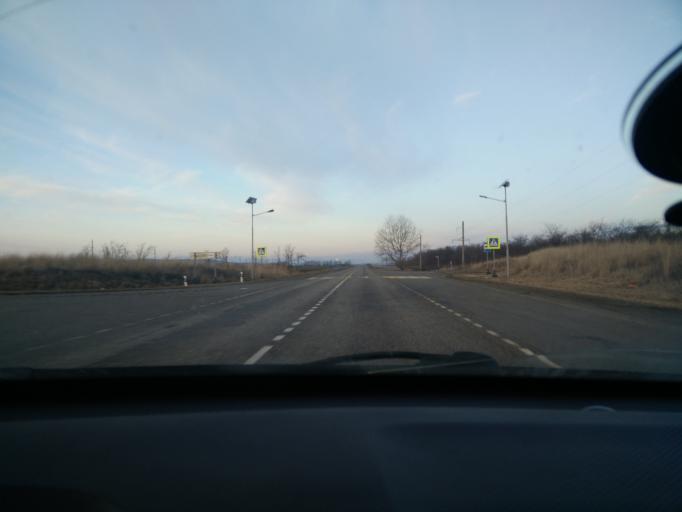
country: RU
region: Stavropol'skiy
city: Tatarka
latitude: 44.9966
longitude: 41.7496
